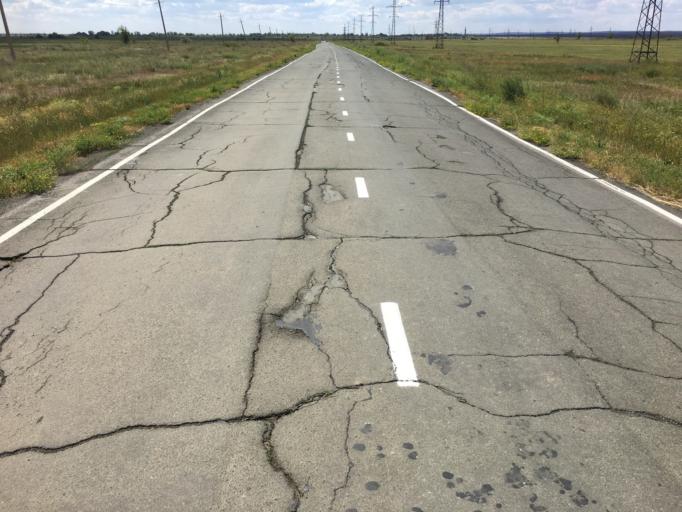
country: RU
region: Orenburg
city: Novotroitsk
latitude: 51.1556
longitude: 58.3407
